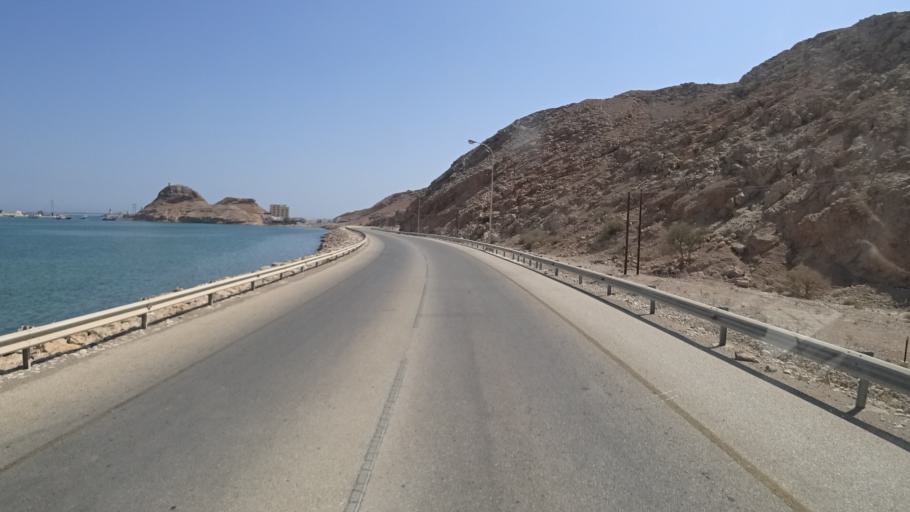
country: OM
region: Ash Sharqiyah
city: Sur
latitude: 22.5544
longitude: 59.5378
